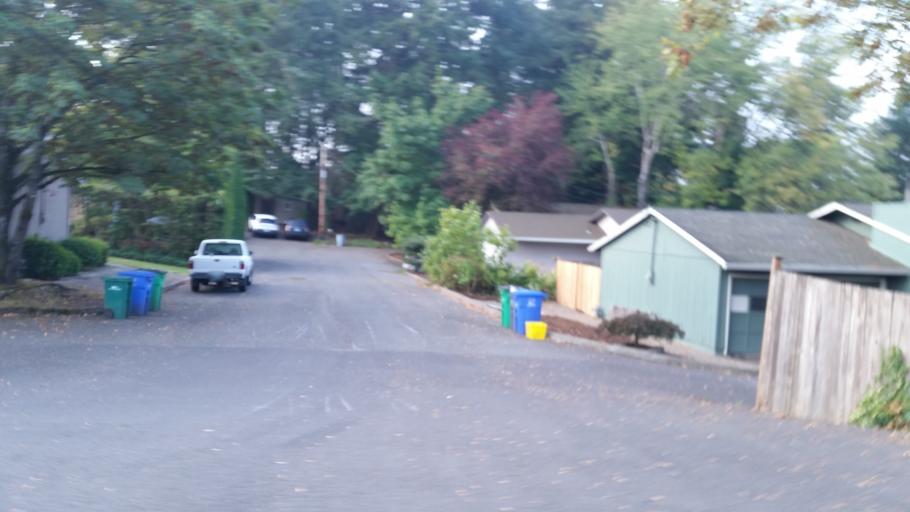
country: US
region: Oregon
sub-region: Washington County
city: Garden Home-Whitford
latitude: 45.4662
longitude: -122.7073
